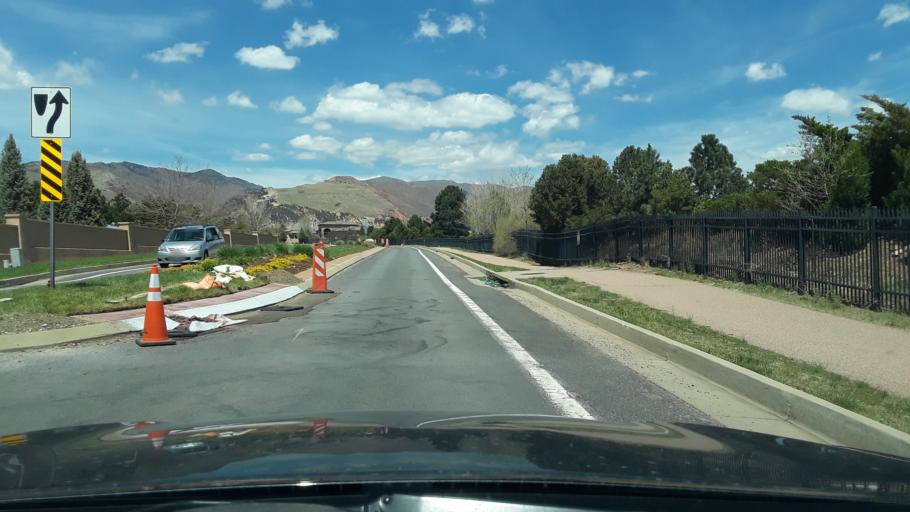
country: US
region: Colorado
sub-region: El Paso County
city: Manitou Springs
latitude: 38.8809
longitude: -104.8684
